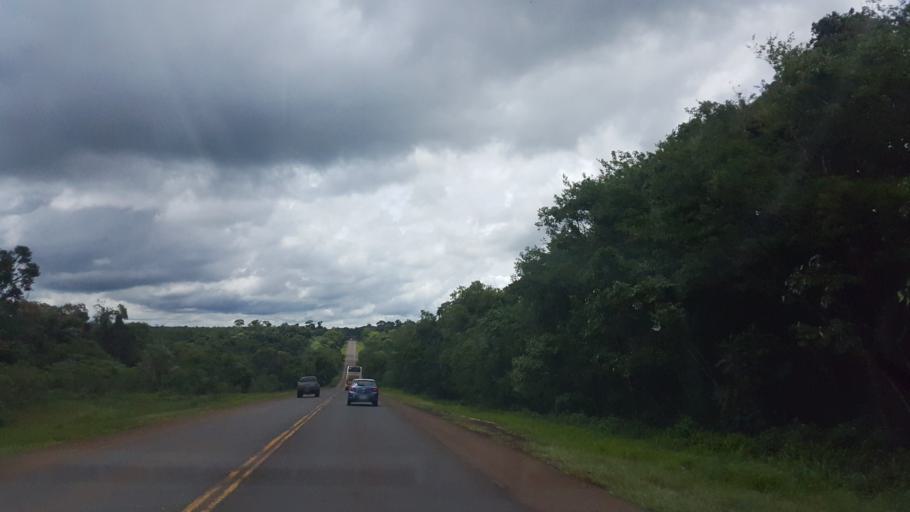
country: AR
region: Misiones
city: Puerto Libertad
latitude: -25.8045
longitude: -54.5387
